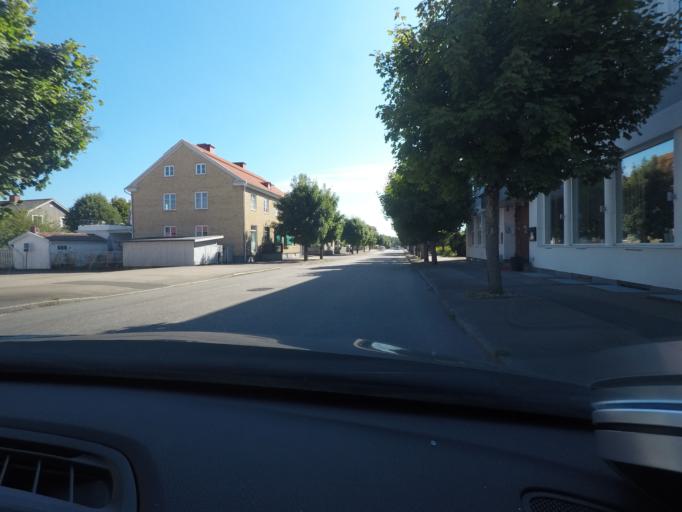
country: SE
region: Kronoberg
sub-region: Markaryds Kommun
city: Markaryd
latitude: 56.4598
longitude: 13.5954
